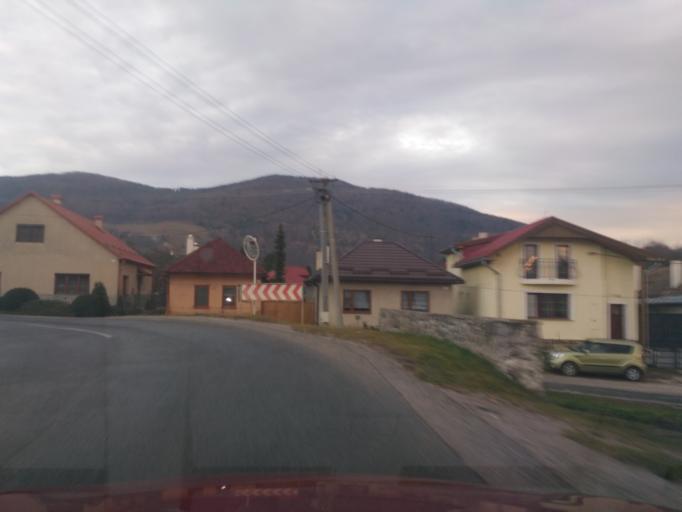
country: SK
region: Kosicky
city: Gelnica
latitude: 48.8283
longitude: 20.8684
